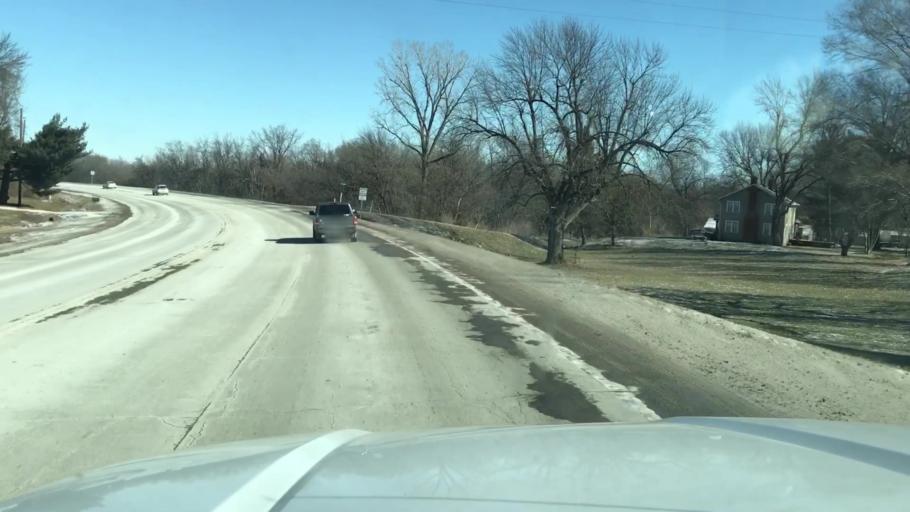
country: US
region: Missouri
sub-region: Andrew County
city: Country Club Village
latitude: 39.8036
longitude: -94.8125
